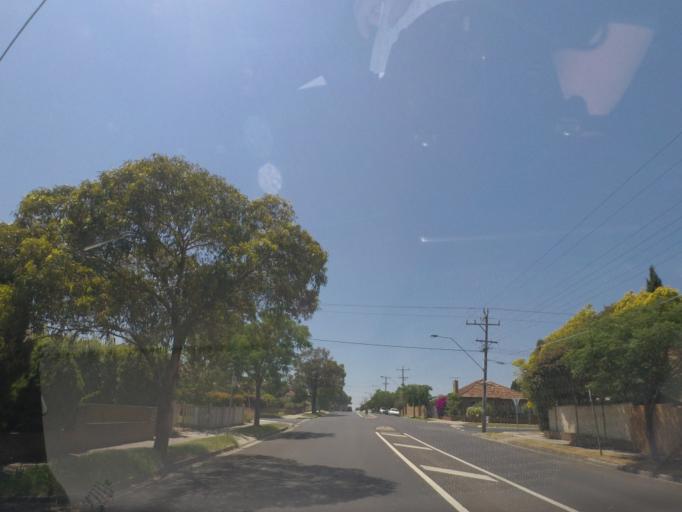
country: AU
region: Victoria
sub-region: Moreland
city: Pascoe Vale
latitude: -37.7268
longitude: 144.9391
